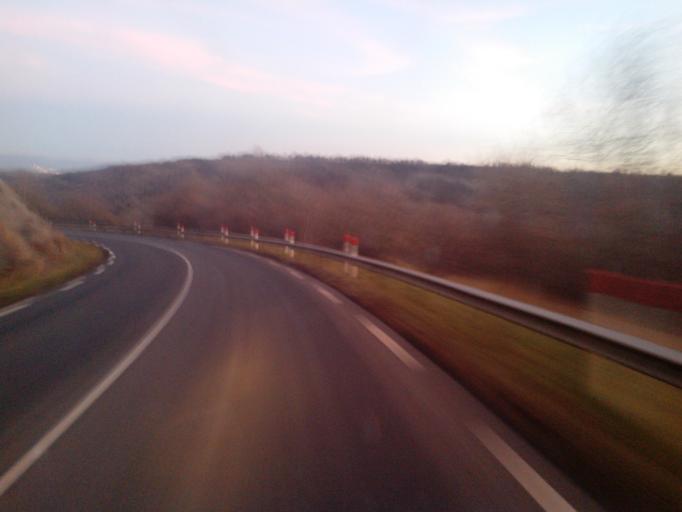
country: FR
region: Auvergne
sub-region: Departement du Cantal
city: Saint-Flour
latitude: 45.0529
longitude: 3.0140
